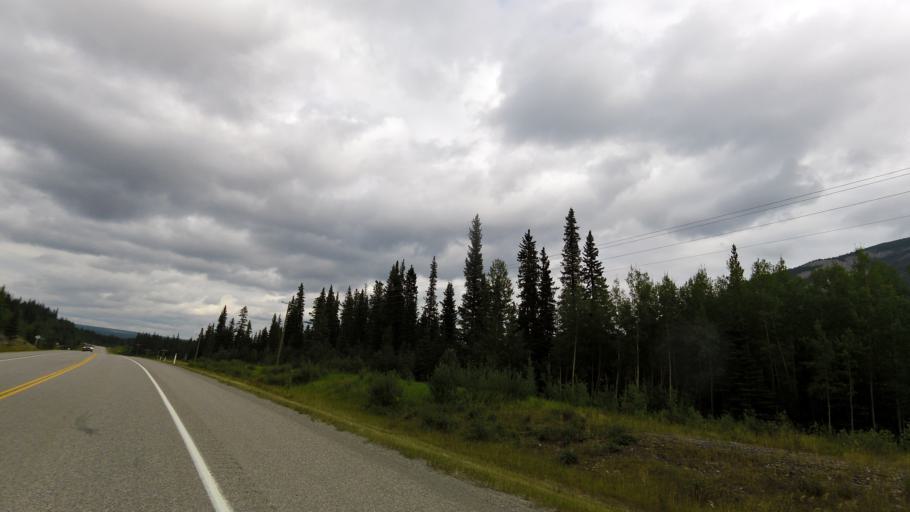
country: CA
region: Alberta
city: Rocky Mountain House
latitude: 52.4922
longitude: -116.0162
